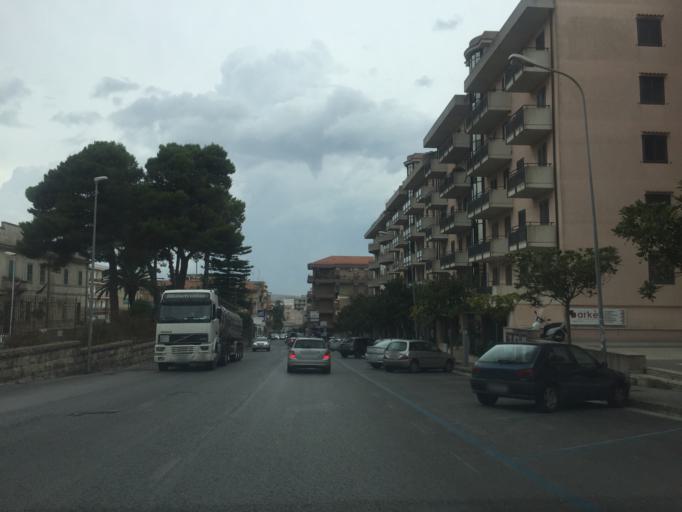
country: IT
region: Sicily
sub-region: Ragusa
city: Ragusa
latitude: 36.9137
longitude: 14.7246
